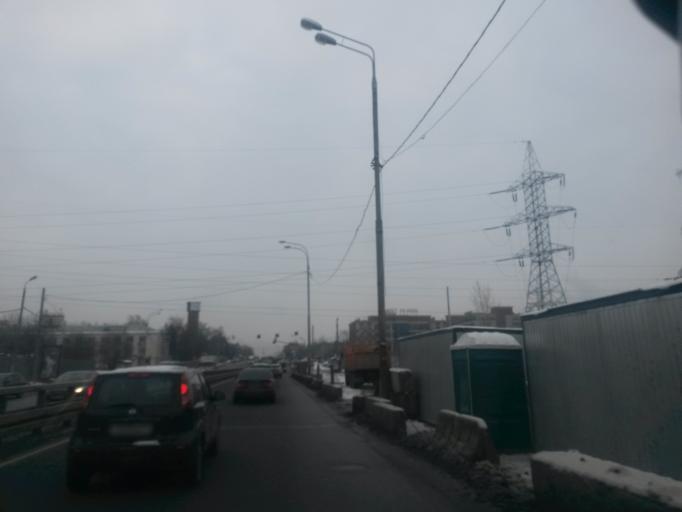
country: RU
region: Moskovskaya
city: Bol'shaya Setun'
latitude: 55.6990
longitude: 37.4224
